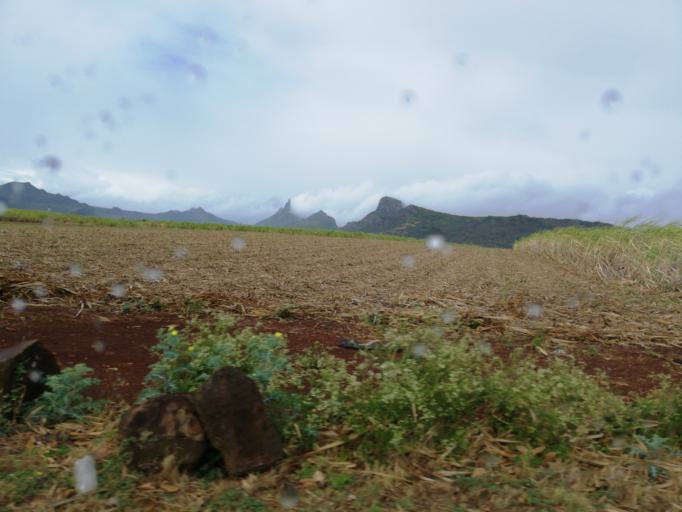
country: MU
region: Pamplemousses
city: Calebasses
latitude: -20.1248
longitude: 57.5619
